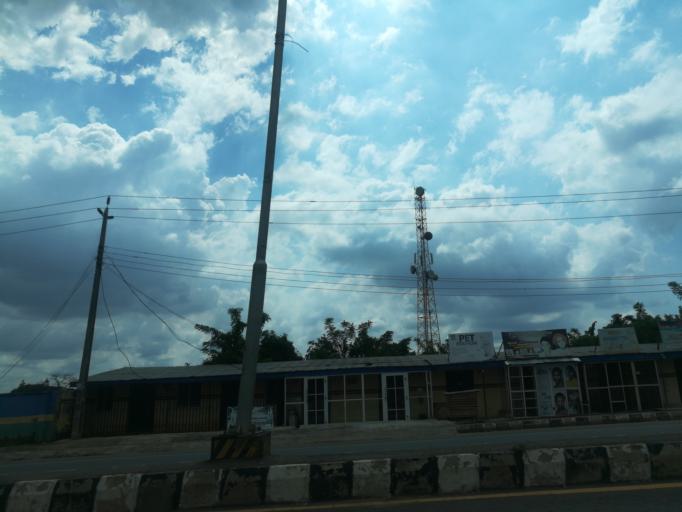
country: NG
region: Oyo
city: Ibadan
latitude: 7.4088
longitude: 3.8679
